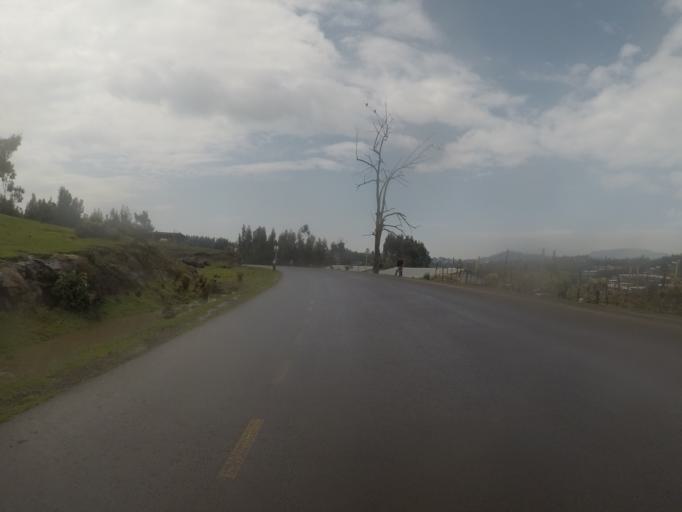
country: ET
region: Amhara
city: Debark'
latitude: 13.1391
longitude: 37.8944
